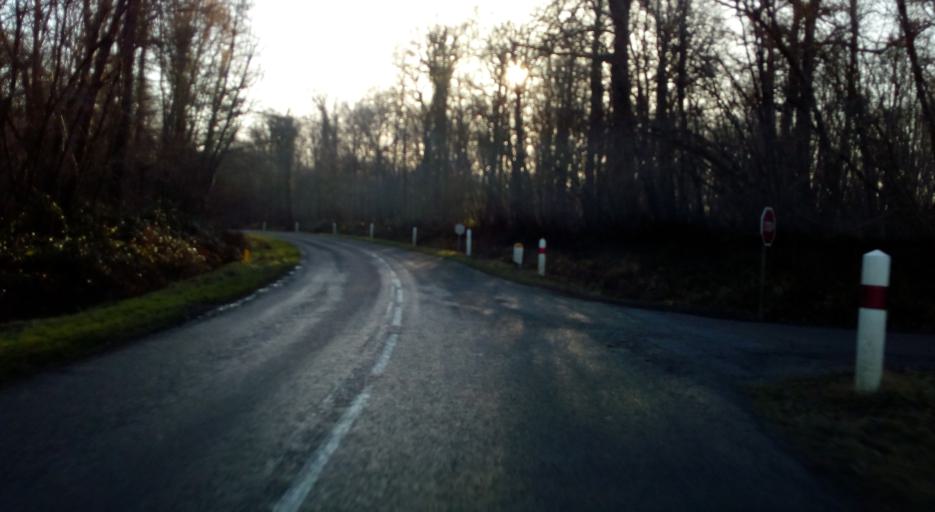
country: FR
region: Champagne-Ardenne
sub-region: Departement des Ardennes
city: Signy-le-Petit
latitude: 49.7765
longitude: 4.3589
